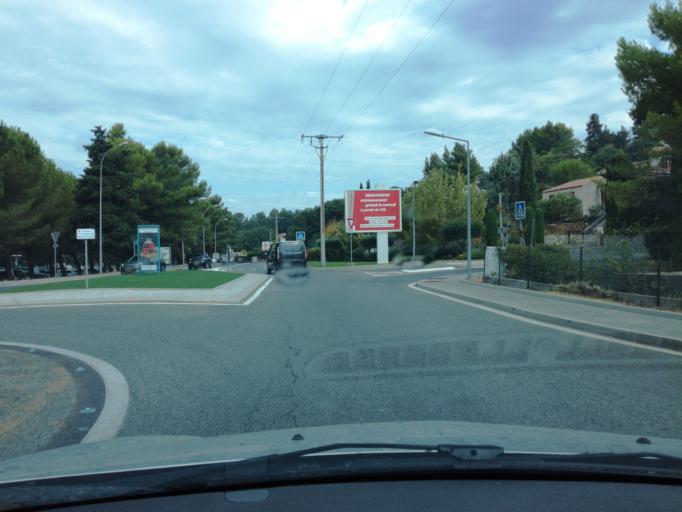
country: FR
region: Provence-Alpes-Cote d'Azur
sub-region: Departement du Var
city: Draguignan
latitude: 43.5249
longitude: 6.4607
